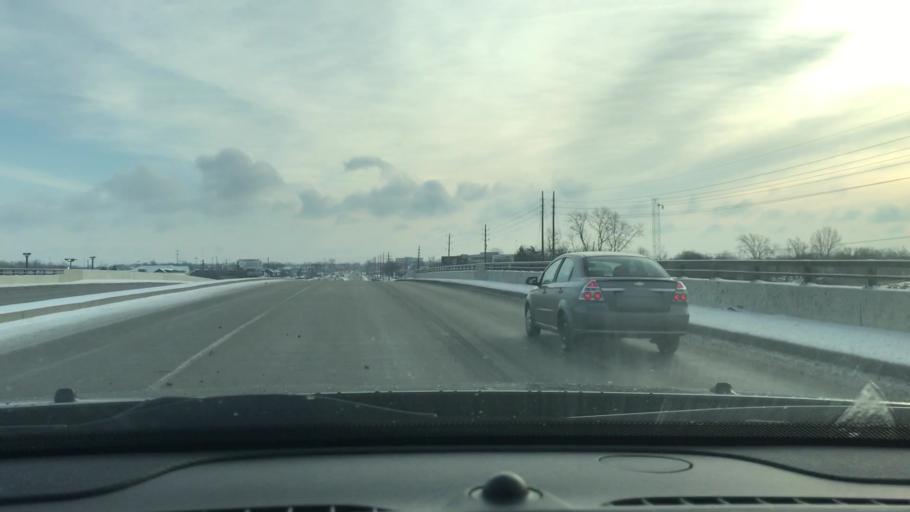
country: US
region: Indiana
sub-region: Hamilton County
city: Fishers
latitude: 39.9050
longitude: -86.0707
